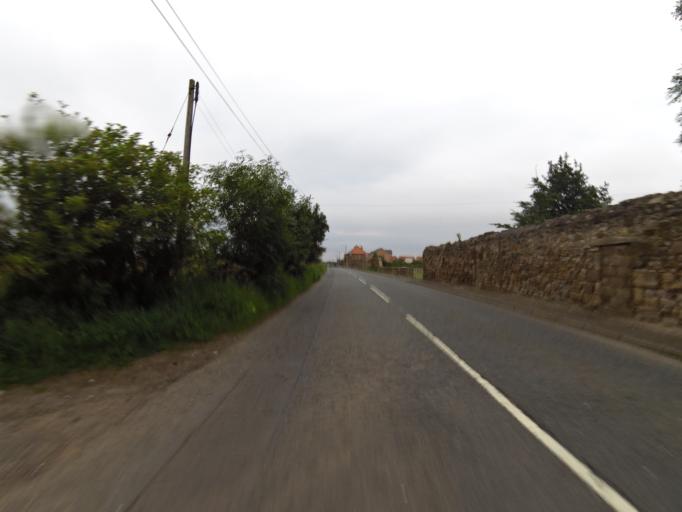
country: GB
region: Scotland
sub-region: East Lothian
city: Musselburgh
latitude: 55.9214
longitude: -3.0686
